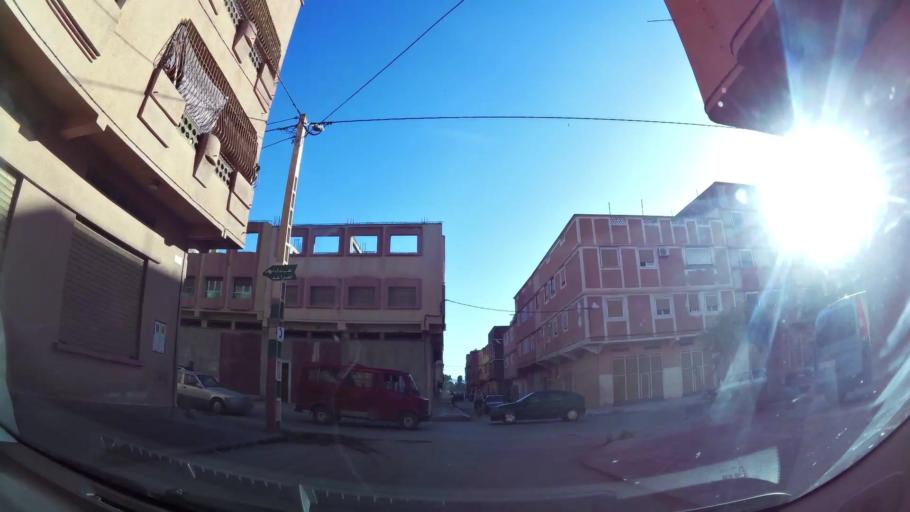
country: MA
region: Oriental
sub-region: Berkane-Taourirt
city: Berkane
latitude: 34.9265
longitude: -2.3395
